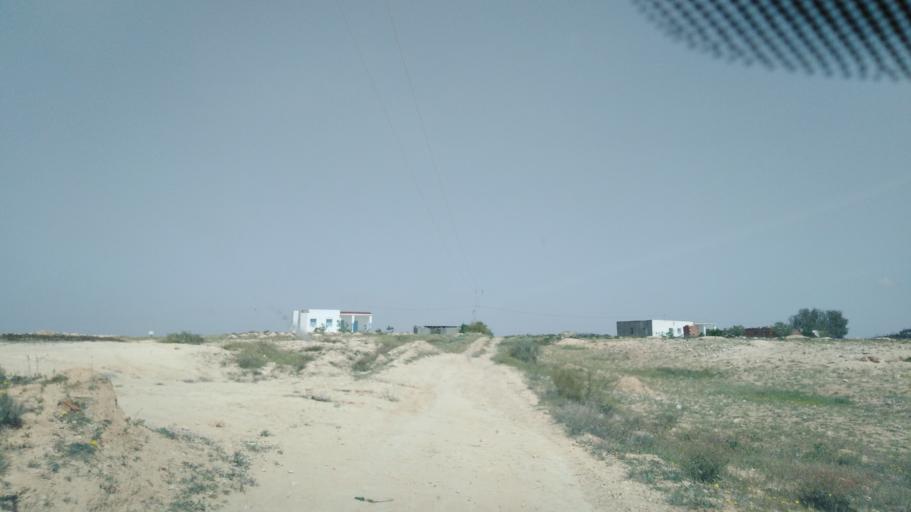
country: TN
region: Safaqis
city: Sfax
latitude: 34.7455
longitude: 10.5693
